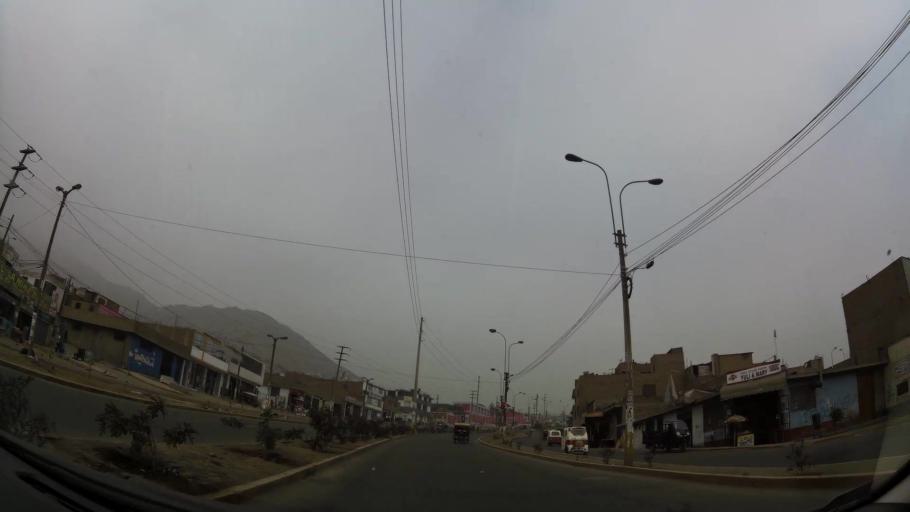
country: PE
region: Lima
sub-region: Lima
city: Chaclacayo
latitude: -12.0102
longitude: -76.8217
